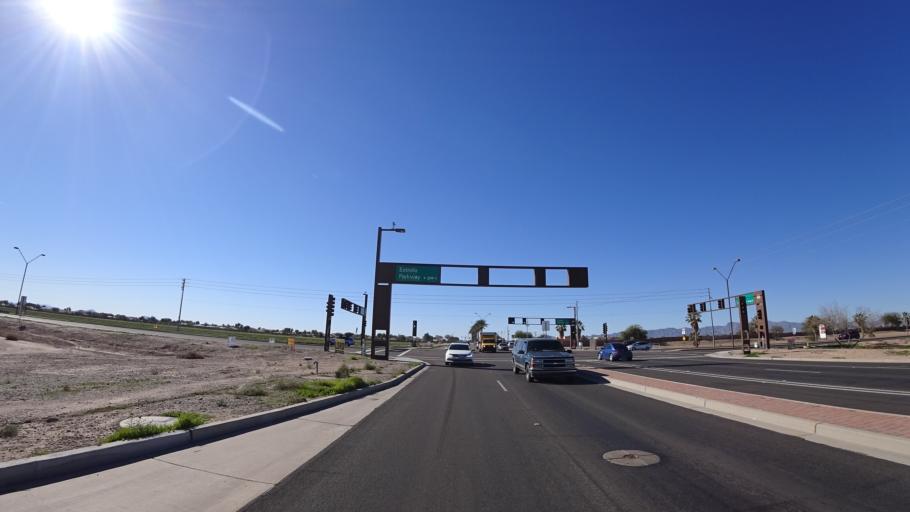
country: US
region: Arizona
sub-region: Maricopa County
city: Goodyear
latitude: 33.4355
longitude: -112.3921
